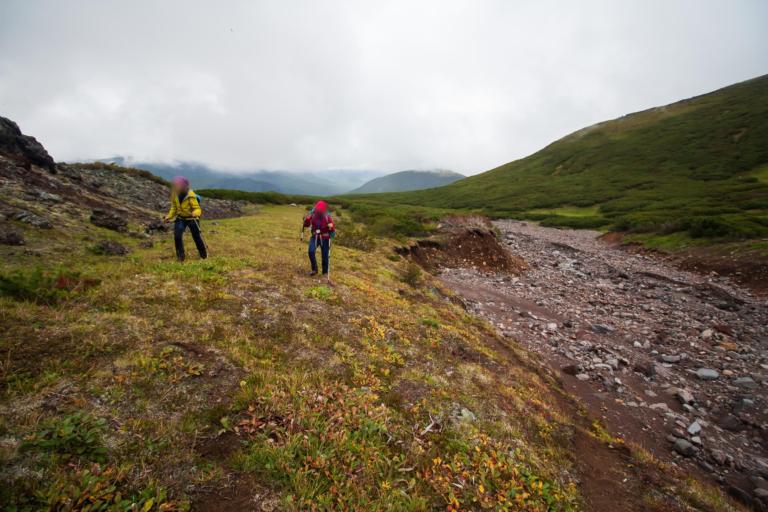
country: RU
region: Kamtsjatka
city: Petropavlovsk-Kamchatsky
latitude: 53.6068
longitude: 158.9371
